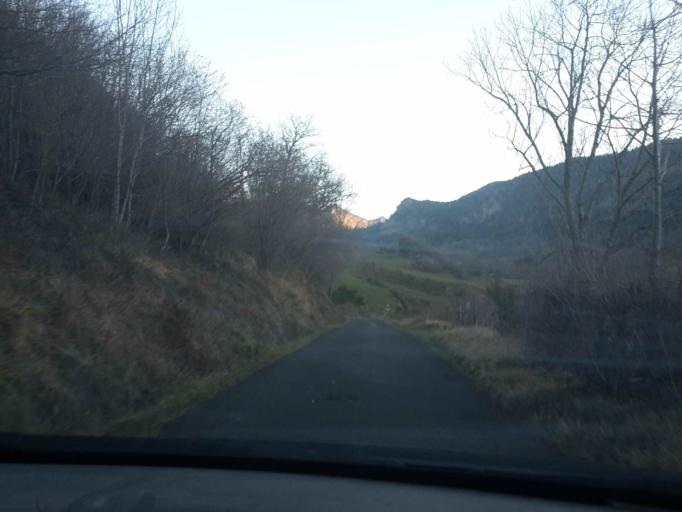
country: FR
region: Auvergne
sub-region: Departement du Cantal
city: Riom-es-Montagnes
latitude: 45.1638
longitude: 2.6103
